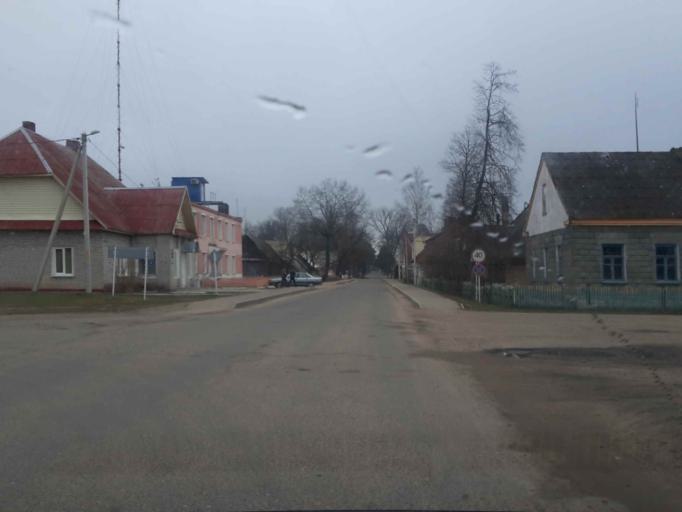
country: BY
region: Vitebsk
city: Mosar
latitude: 55.1421
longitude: 27.2072
